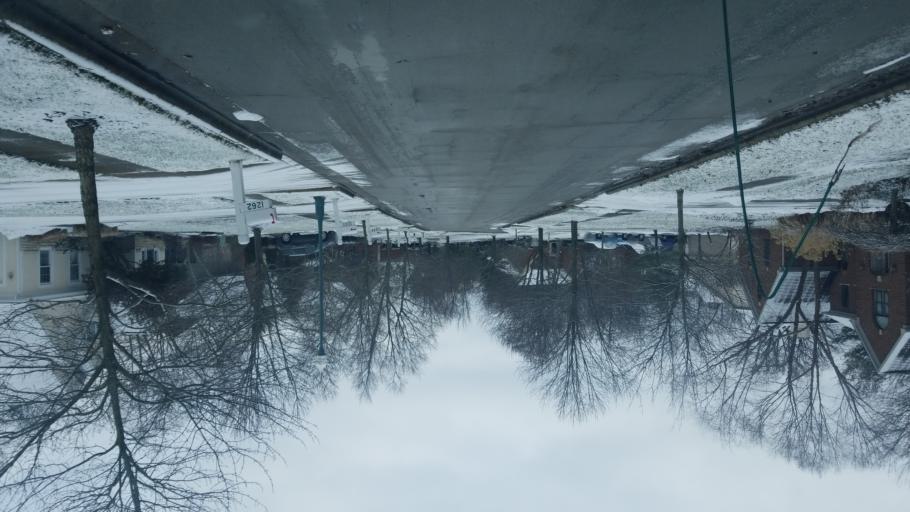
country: US
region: Ohio
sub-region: Franklin County
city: New Albany
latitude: 40.0503
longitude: -82.8338
